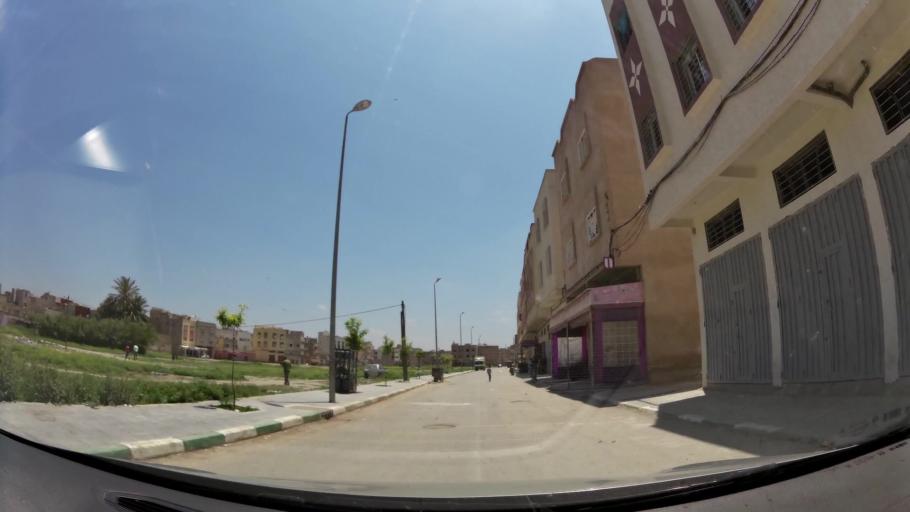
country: MA
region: Fes-Boulemane
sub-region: Fes
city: Fes
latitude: 34.0412
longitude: -5.0511
